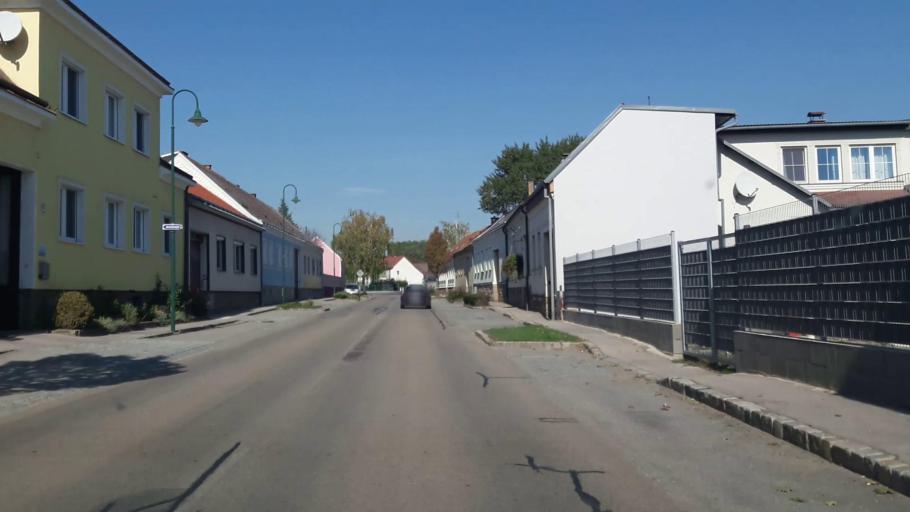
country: AT
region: Lower Austria
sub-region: Politischer Bezirk Korneuburg
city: Harmannsdorf
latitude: 48.3976
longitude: 16.3717
